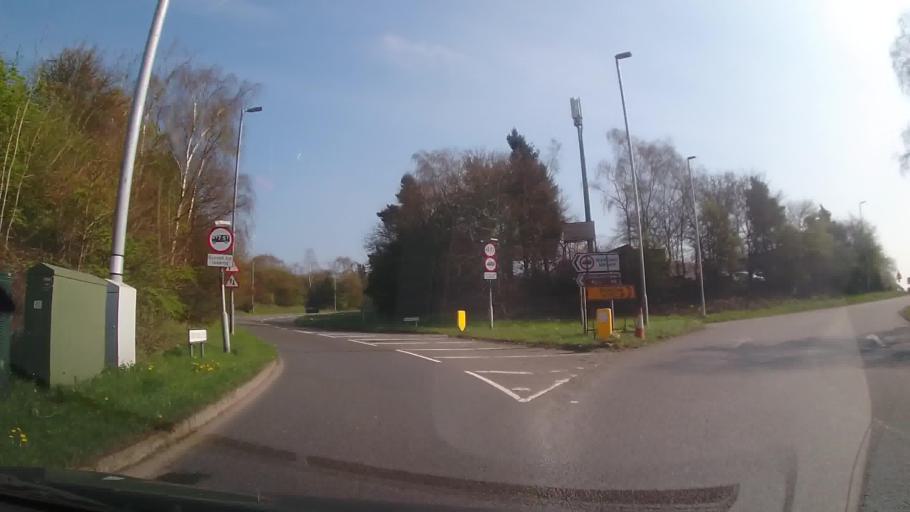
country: GB
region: England
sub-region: Leicestershire
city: Markfield
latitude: 52.6872
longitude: -1.2671
